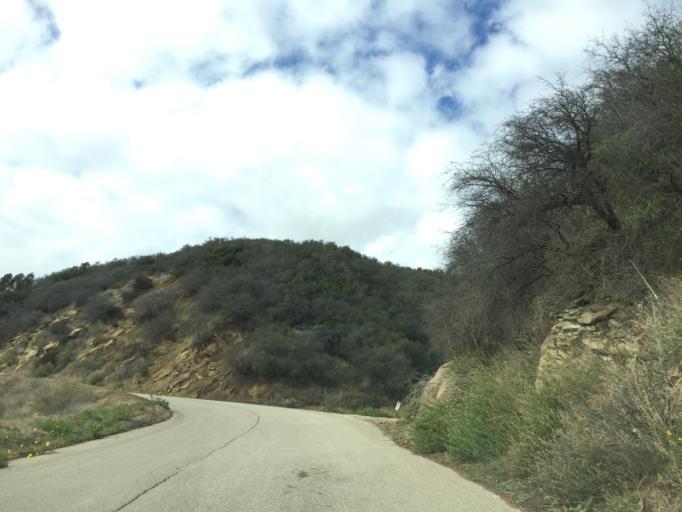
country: US
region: California
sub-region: Santa Barbara County
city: Goleta
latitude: 34.4705
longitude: -119.8009
